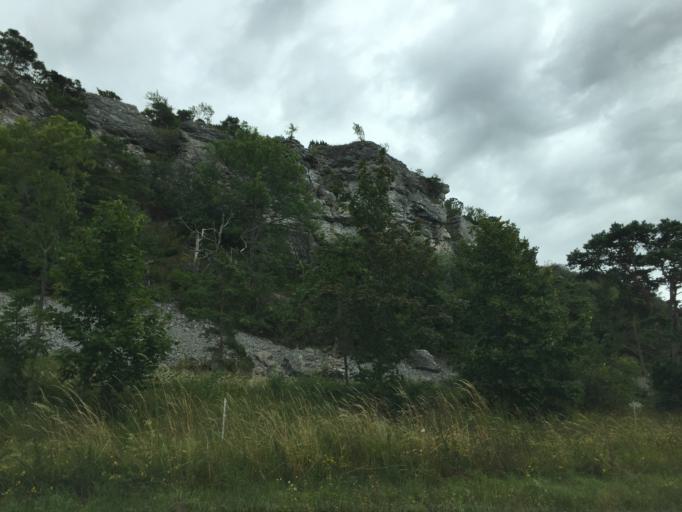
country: SE
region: Gotland
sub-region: Gotland
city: Visby
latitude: 57.7147
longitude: 18.3818
